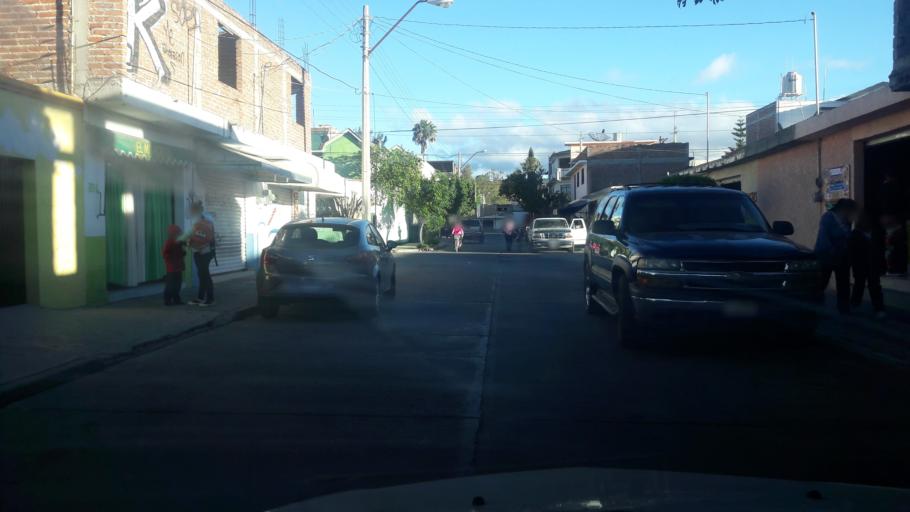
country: MX
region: Guanajuato
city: Leon
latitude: 21.1774
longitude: -101.6687
